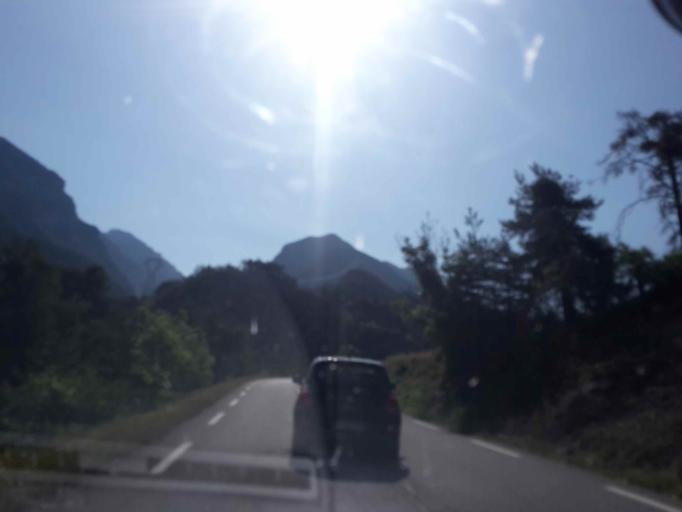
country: FR
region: Provence-Alpes-Cote d'Azur
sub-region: Departement des Hautes-Alpes
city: Guillestre
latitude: 44.6456
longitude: 6.6576
